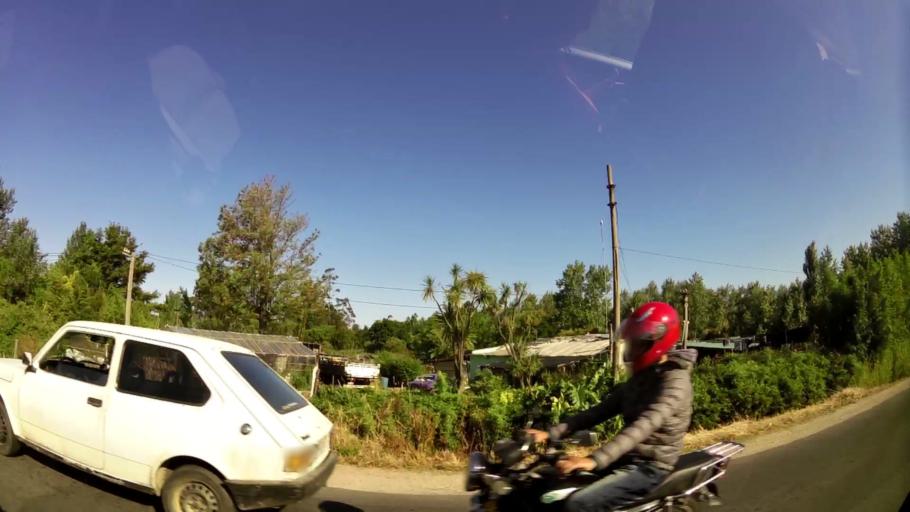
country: UY
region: Canelones
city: La Paz
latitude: -34.8156
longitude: -56.1713
